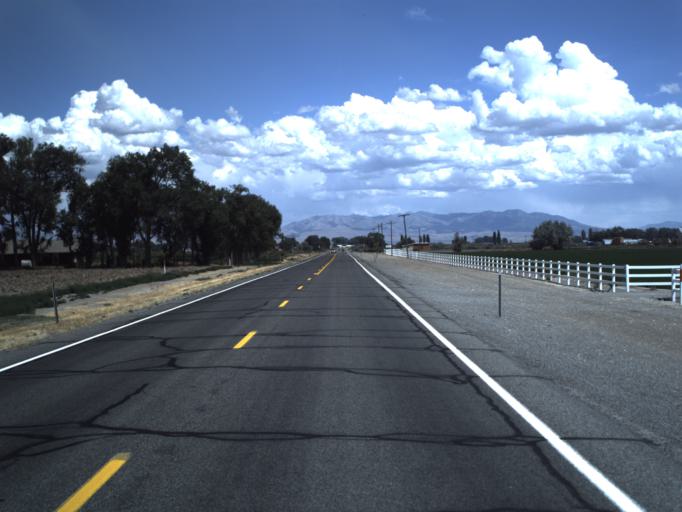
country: US
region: Utah
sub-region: Millard County
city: Delta
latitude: 39.3305
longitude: -112.6293
